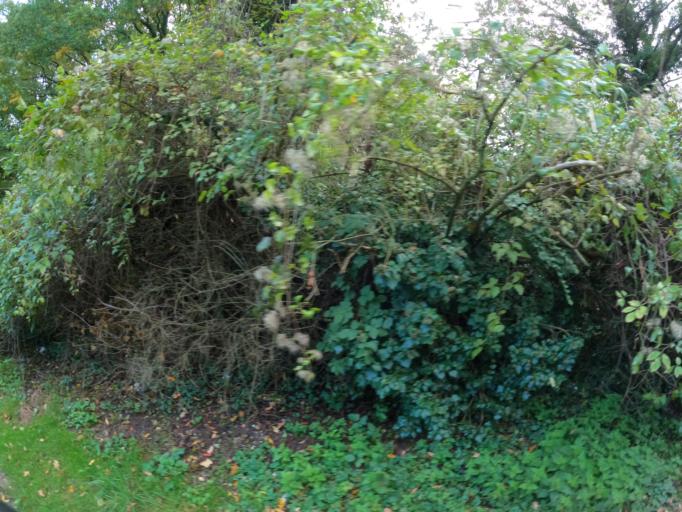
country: FR
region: Ile-de-France
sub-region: Departement de Seine-et-Marne
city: Saint-Germain-sur-Morin
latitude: 48.8744
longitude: 2.8540
